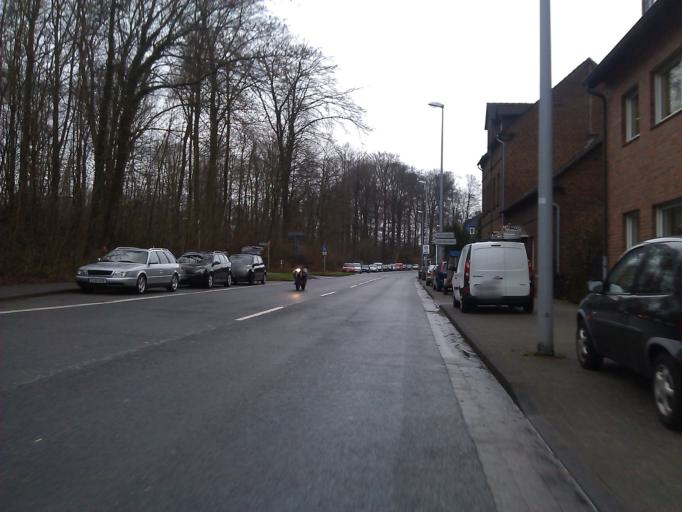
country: DE
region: North Rhine-Westphalia
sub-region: Regierungsbezirk Dusseldorf
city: Heiligenhaus
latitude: 51.3705
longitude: 6.9347
